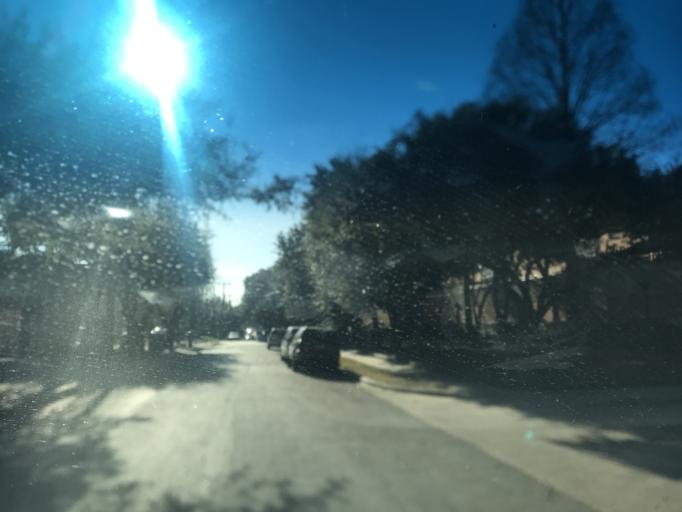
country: US
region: Texas
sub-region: Dallas County
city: Highland Park
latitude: 32.8221
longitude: -96.8120
